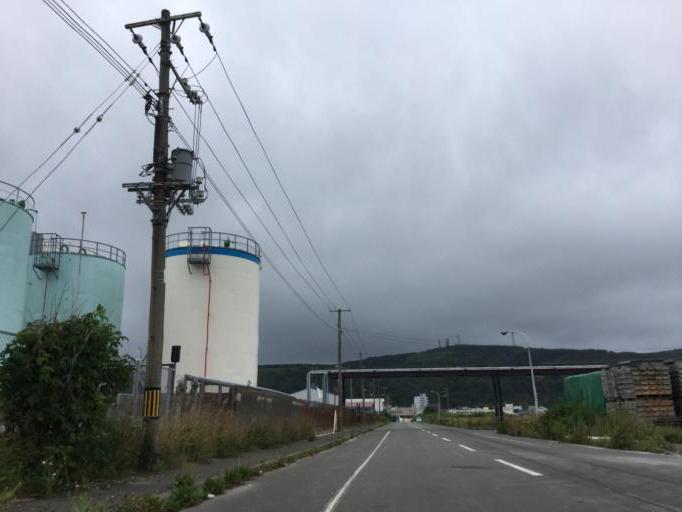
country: JP
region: Hokkaido
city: Wakkanai
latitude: 45.4094
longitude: 141.6848
